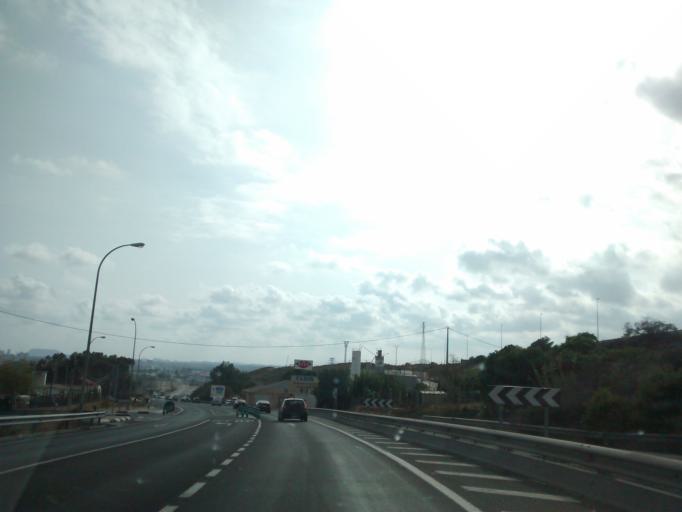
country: ES
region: Valencia
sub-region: Provincia de Alicante
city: el Campello
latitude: 38.4541
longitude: -0.3687
